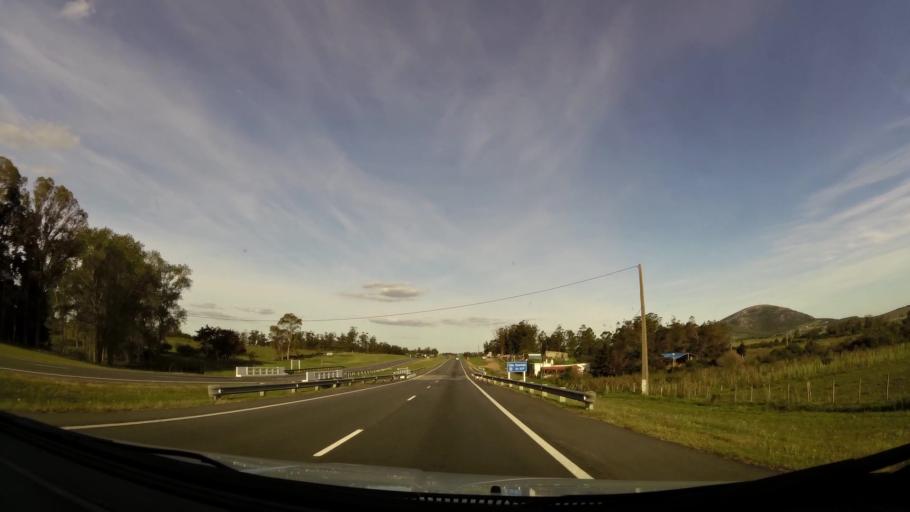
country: UY
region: Maldonado
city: Pan de Azucar
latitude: -34.7899
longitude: -55.3022
